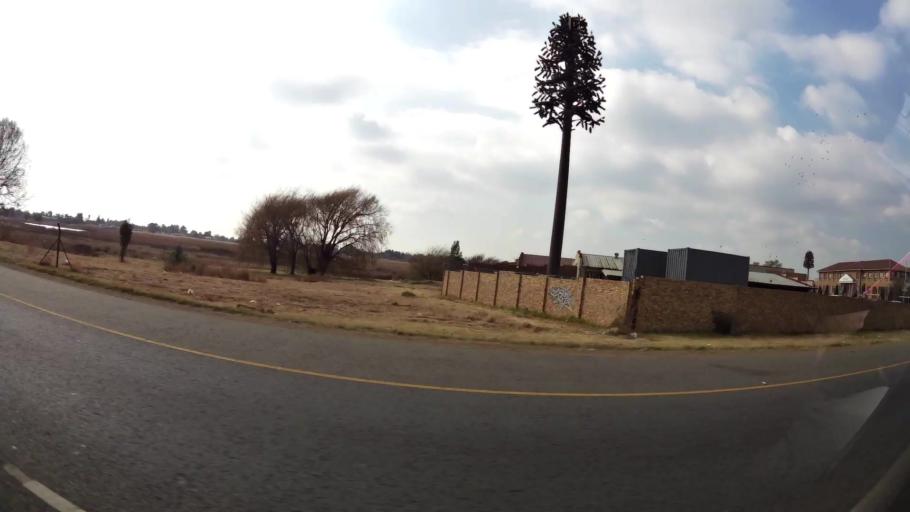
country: ZA
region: Gauteng
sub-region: Ekurhuleni Metropolitan Municipality
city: Boksburg
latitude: -26.1177
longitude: 28.2564
